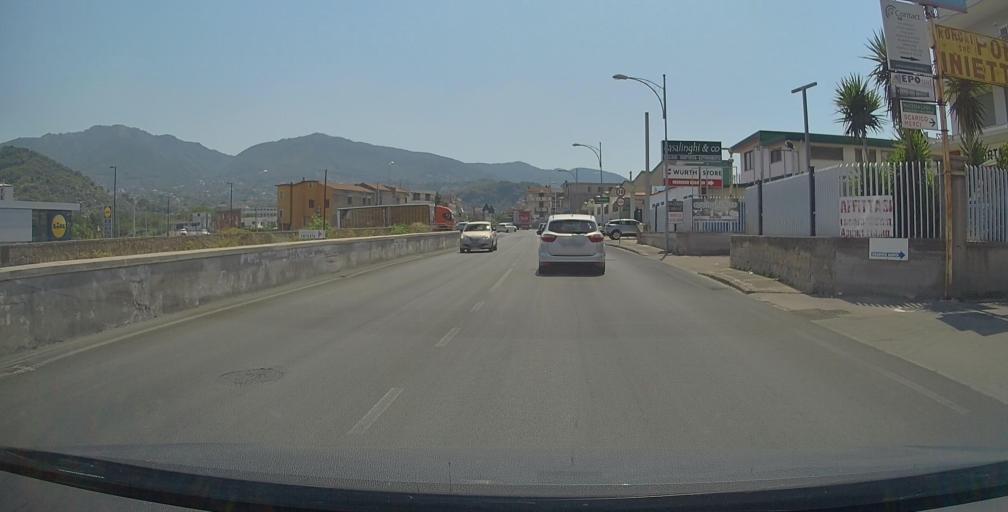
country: IT
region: Campania
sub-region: Provincia di Salerno
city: Nocera Superiore
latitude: 40.7351
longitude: 14.6819
